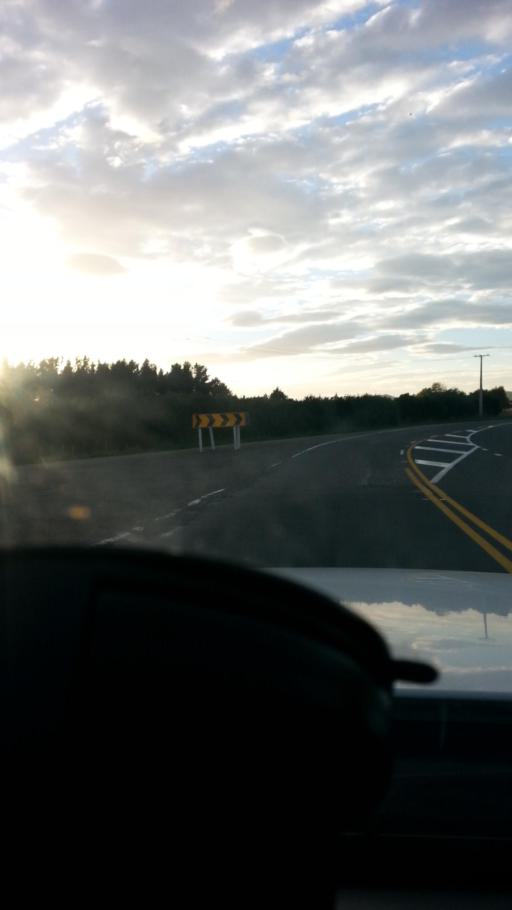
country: NZ
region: Wellington
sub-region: Masterton District
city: Masterton
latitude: -40.9498
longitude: 175.6958
